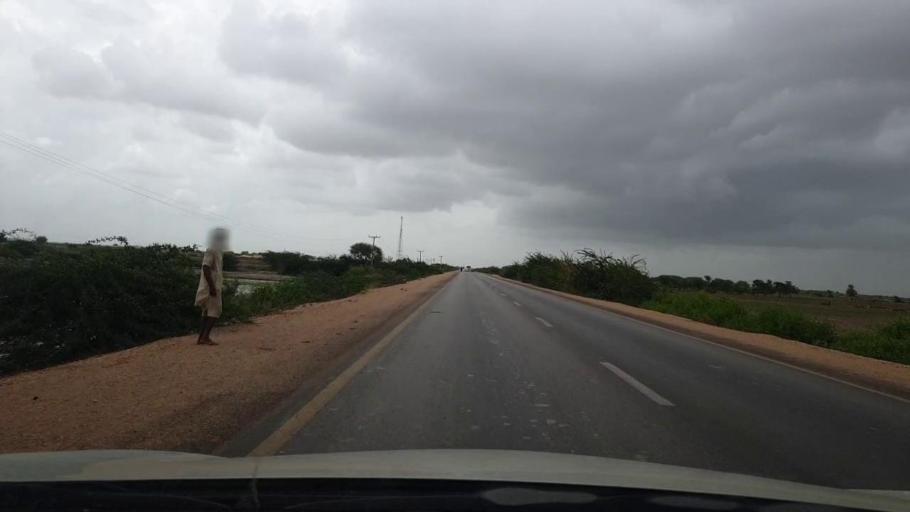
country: PK
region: Sindh
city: Mirpur Batoro
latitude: 24.6440
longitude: 68.4242
